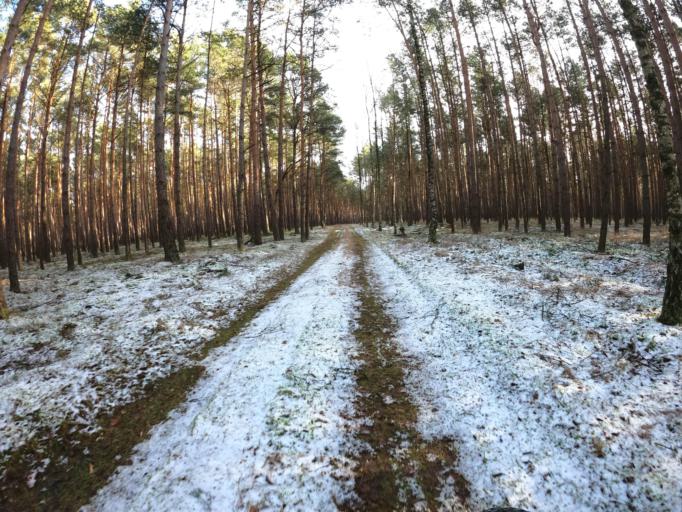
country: PL
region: Lubusz
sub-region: Powiat slubicki
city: Cybinka
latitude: 52.2424
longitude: 14.8197
